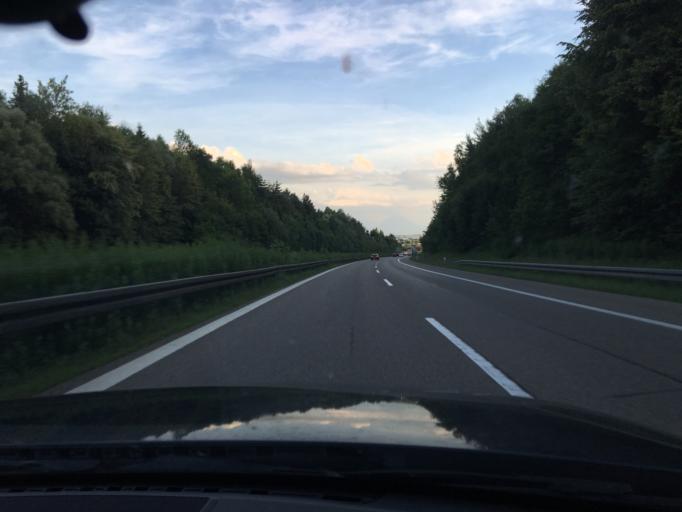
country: AT
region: Vorarlberg
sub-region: Politischer Bezirk Bregenz
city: Horbranz
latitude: 47.5613
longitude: 9.7372
